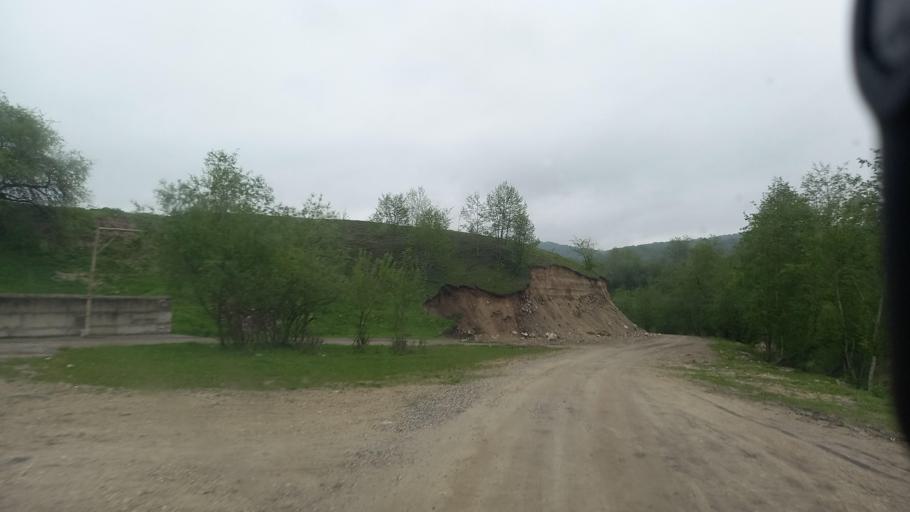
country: RU
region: Kabardino-Balkariya
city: Babugent
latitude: 43.2496
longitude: 43.5300
